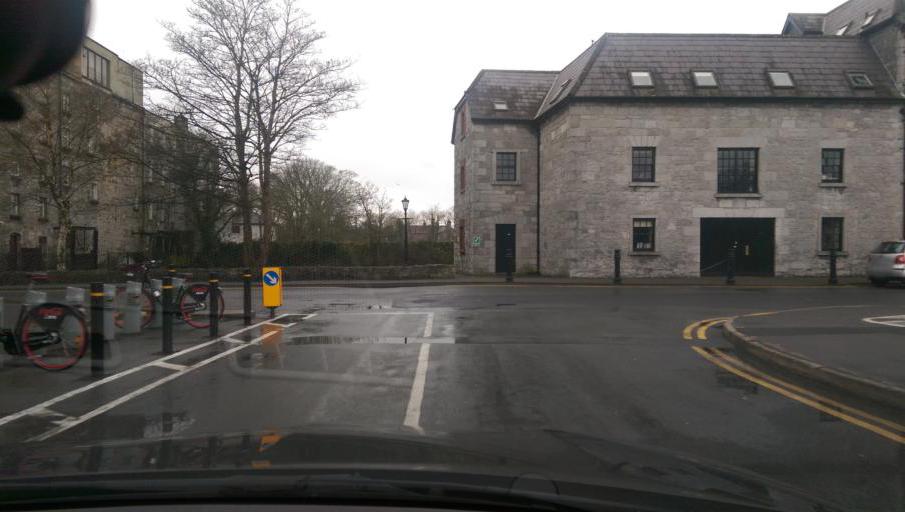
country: IE
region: Connaught
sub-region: County Galway
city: Gaillimh
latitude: 53.2738
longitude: -9.0570
